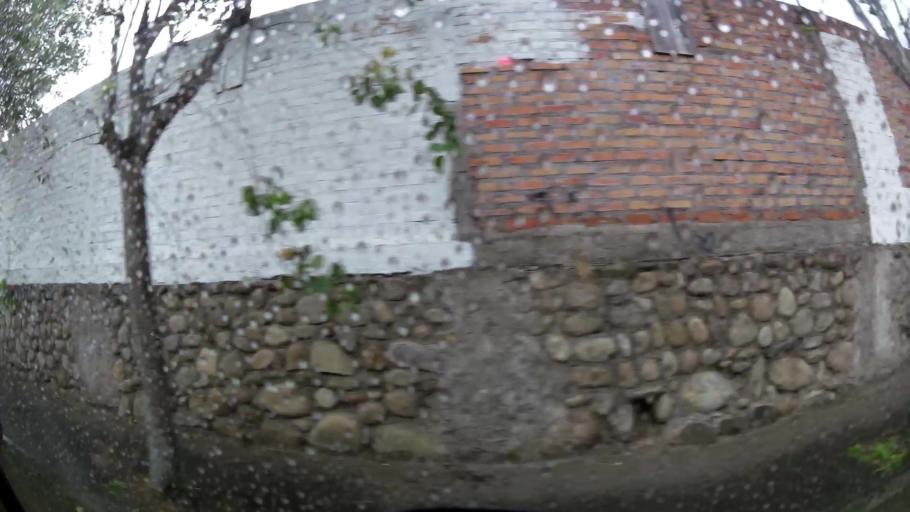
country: EC
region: Azuay
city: Cuenca
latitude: -2.8929
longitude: -79.0328
